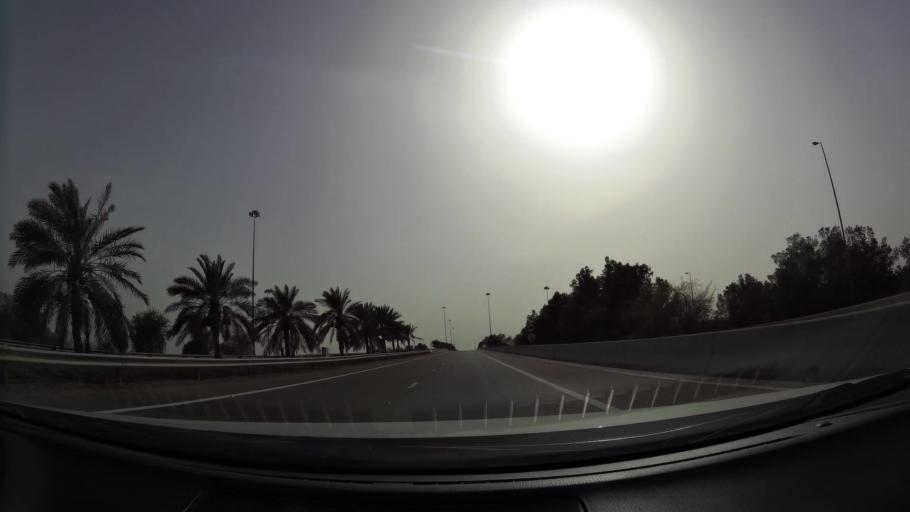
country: AE
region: Abu Dhabi
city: Al Ain
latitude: 24.2000
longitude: 55.5862
